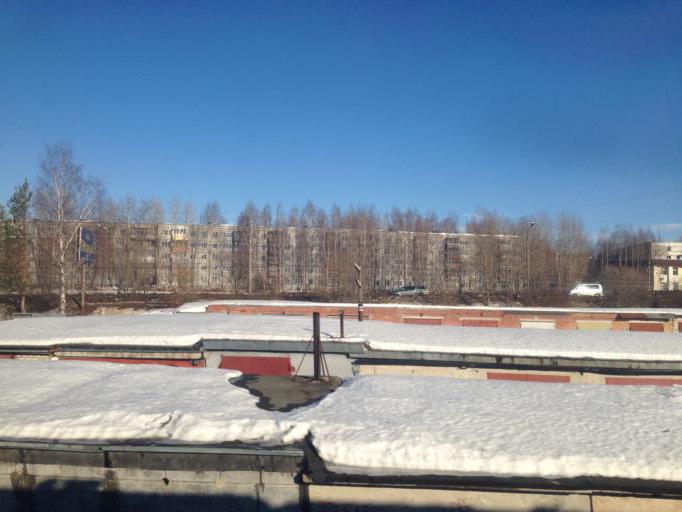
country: RU
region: Komi Republic
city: Ezhva
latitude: 61.7928
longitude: 50.7388
